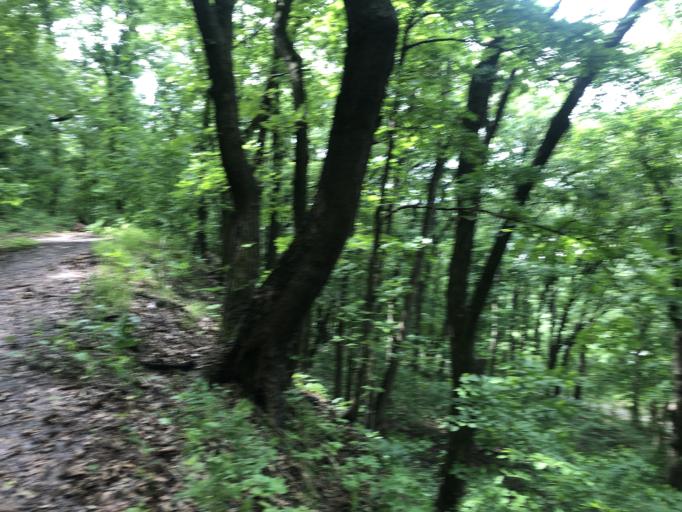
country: US
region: Missouri
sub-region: Platte County
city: Weston
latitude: 39.3863
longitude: -94.8801
